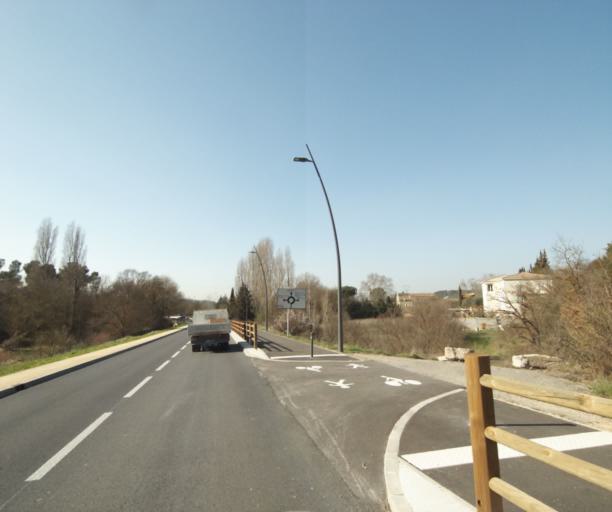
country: FR
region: Provence-Alpes-Cote d'Azur
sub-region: Departement des Bouches-du-Rhone
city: Bouc-Bel-Air
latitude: 43.4475
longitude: 5.4004
